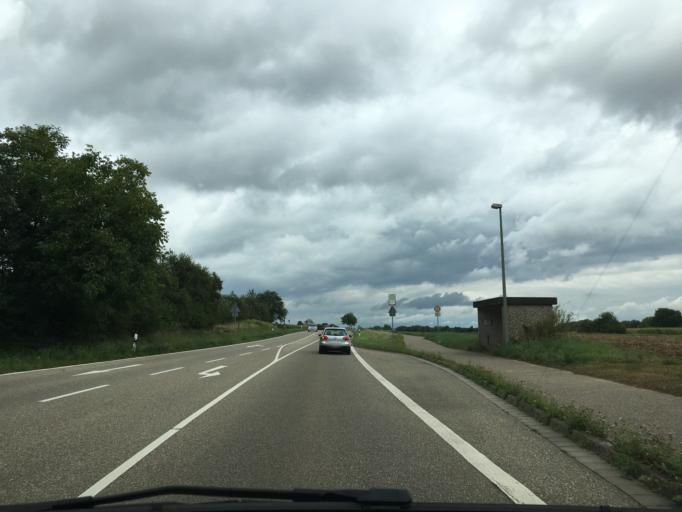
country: DE
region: Rheinland-Pfalz
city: Niederotterbach
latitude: 49.0533
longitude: 8.0456
